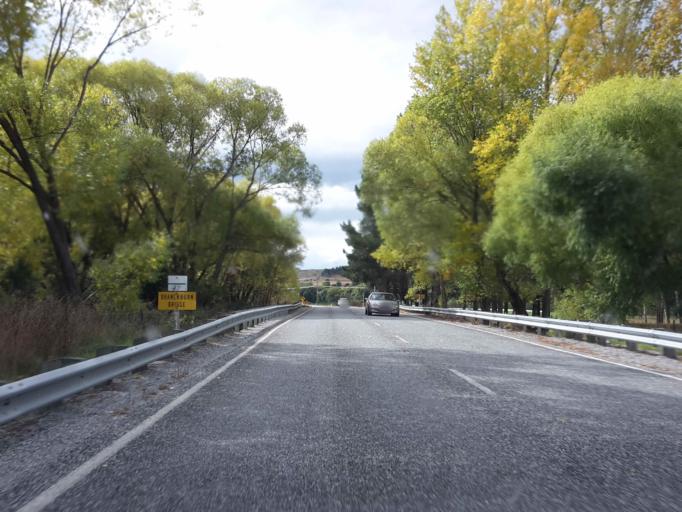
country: NZ
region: Otago
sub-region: Queenstown-Lakes District
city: Wanaka
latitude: -44.8328
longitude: 169.0579
